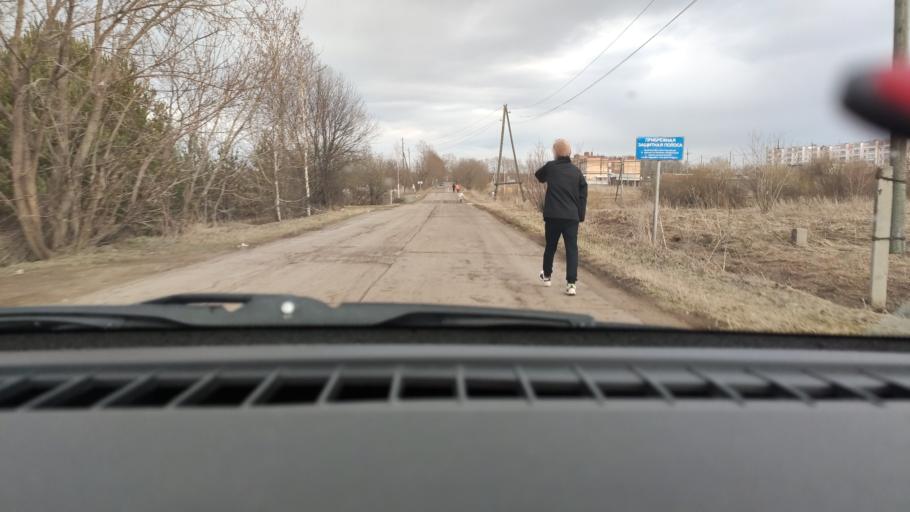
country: RU
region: Perm
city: Gamovo
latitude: 57.8746
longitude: 56.0938
